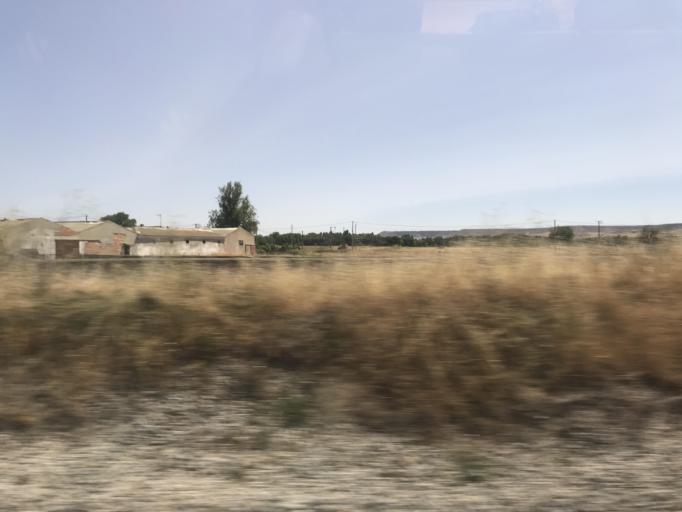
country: ES
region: Castille and Leon
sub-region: Provincia de Valladolid
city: Cubillas de Santa Marta
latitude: 41.8158
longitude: -4.5751
